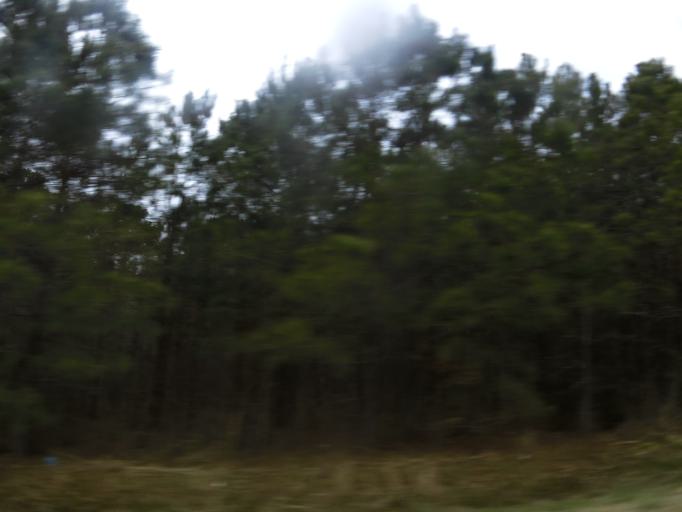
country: US
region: North Carolina
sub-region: Hertford County
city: Murfreesboro
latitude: 36.3440
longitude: -77.1978
